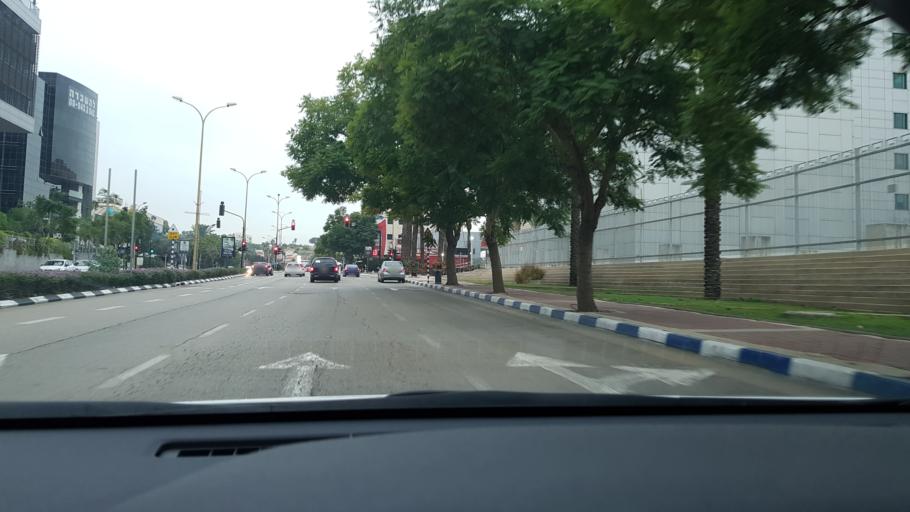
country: IL
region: Central District
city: Ness Ziona
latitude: 31.9131
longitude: 34.8055
